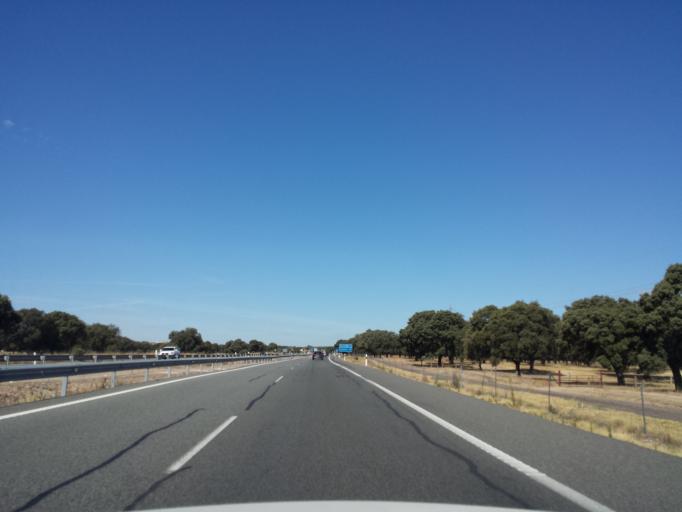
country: ES
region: Castille-La Mancha
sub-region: Province of Toledo
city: Alcanizo
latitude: 39.9245
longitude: -5.1042
